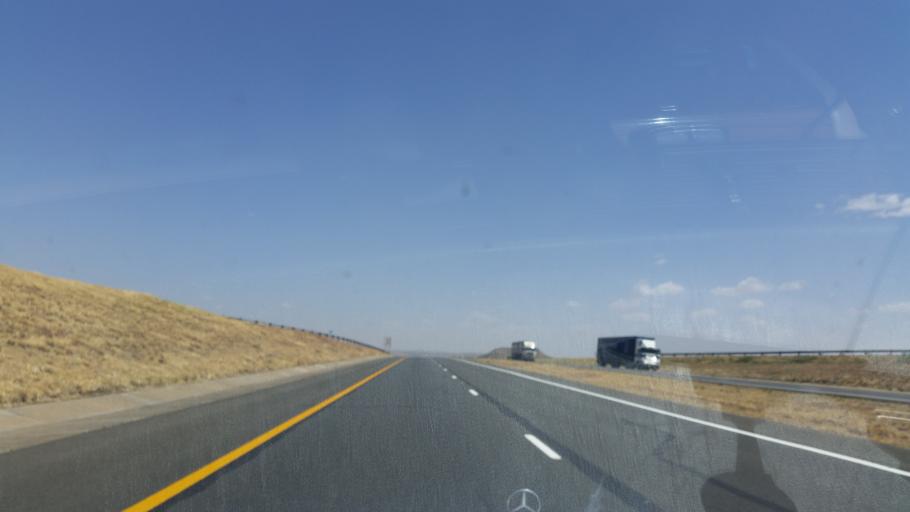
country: ZA
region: Orange Free State
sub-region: Lejweleputswa District Municipality
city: Brandfort
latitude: -28.9343
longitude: 26.4205
